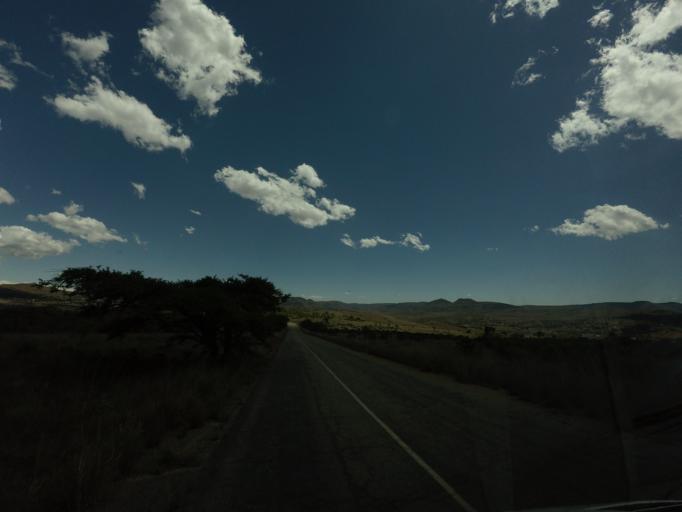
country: ZA
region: Limpopo
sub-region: Mopani District Municipality
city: Hoedspruit
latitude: -24.5840
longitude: 30.7920
